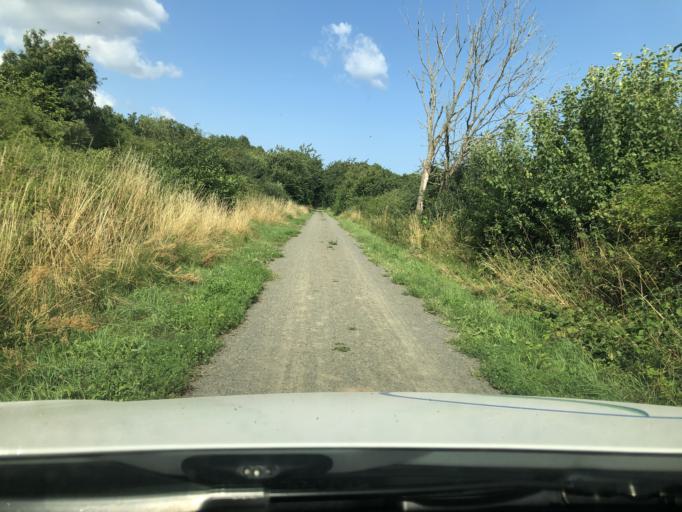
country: SE
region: Skane
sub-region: Kristianstads Kommun
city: Degeberga
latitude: 55.7731
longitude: 14.1607
